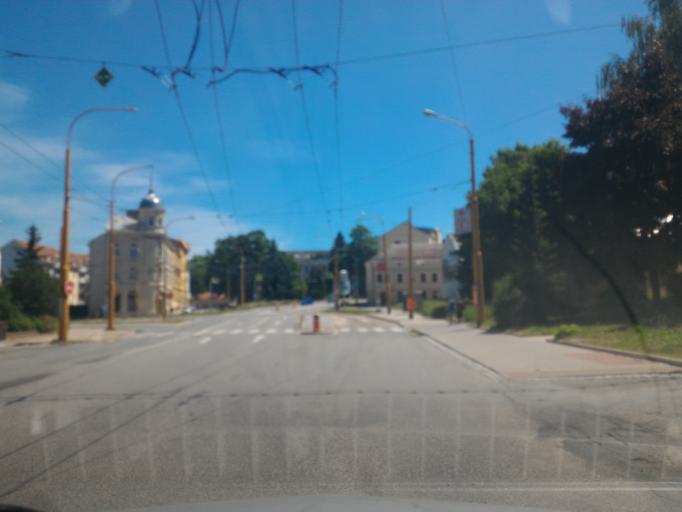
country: CZ
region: Vysocina
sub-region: Okres Jihlava
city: Jihlava
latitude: 49.3996
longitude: 15.5876
